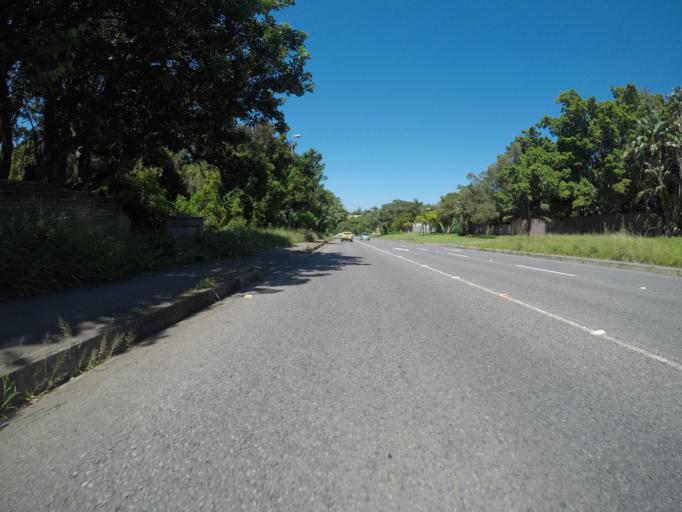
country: ZA
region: Eastern Cape
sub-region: Buffalo City Metropolitan Municipality
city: East London
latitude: -32.9660
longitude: 27.9319
